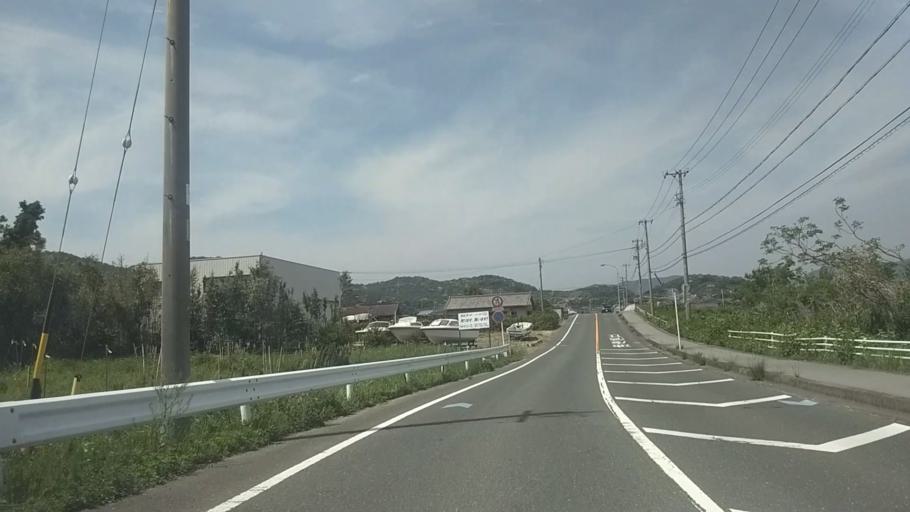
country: JP
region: Shizuoka
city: Kosai-shi
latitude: 34.7805
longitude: 137.5416
